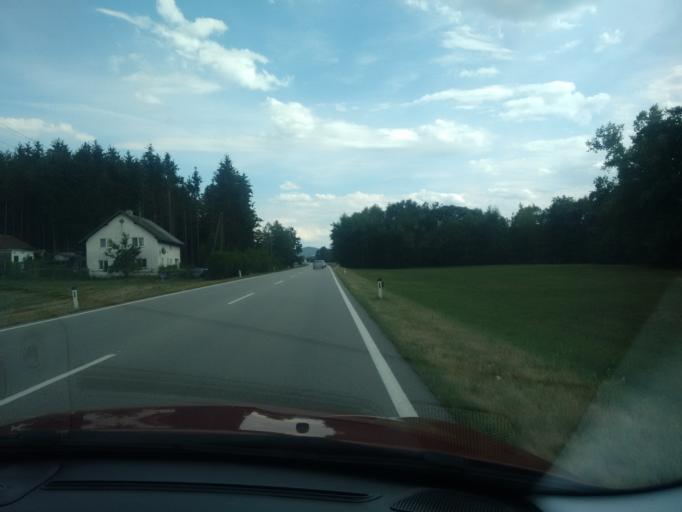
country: AT
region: Upper Austria
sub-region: Politischer Bezirk Ried im Innkreis
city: Ried im Innkreis
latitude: 48.2085
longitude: 13.5266
